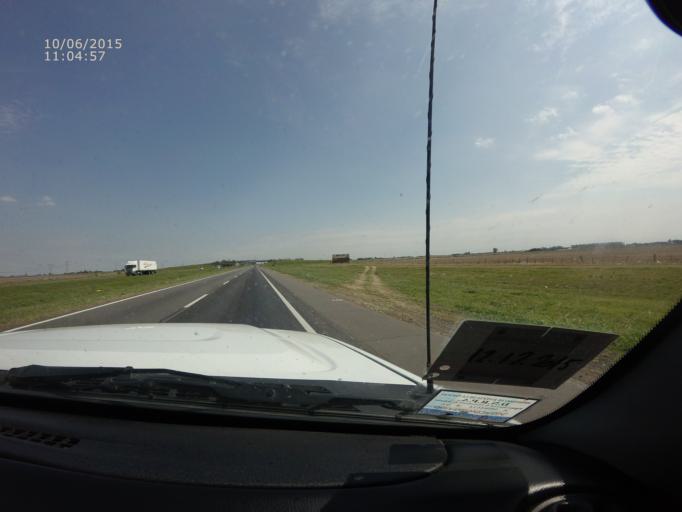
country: AR
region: Santa Fe
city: Arroyo Seco
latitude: -33.2196
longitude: -60.4711
